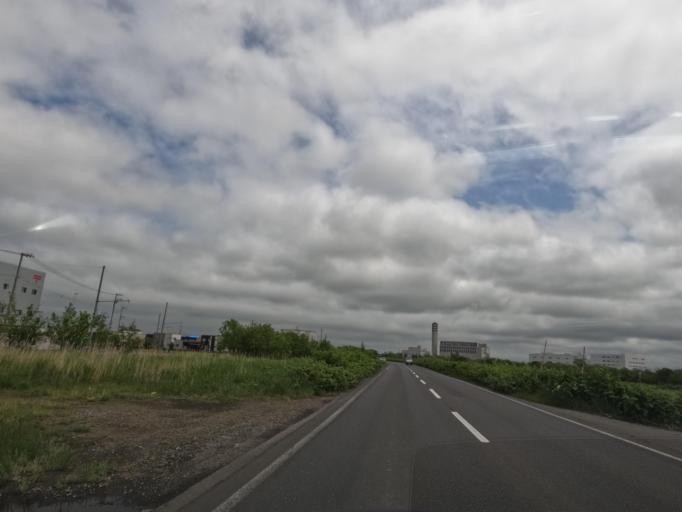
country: JP
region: Hokkaido
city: Sapporo
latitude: 43.0893
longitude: 141.4269
